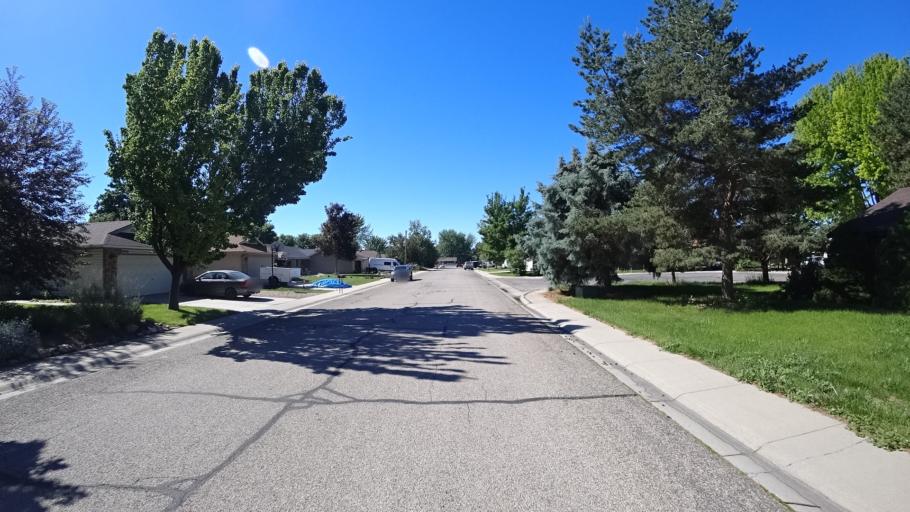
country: US
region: Idaho
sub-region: Ada County
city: Garden City
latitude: 43.6661
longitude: -116.2614
